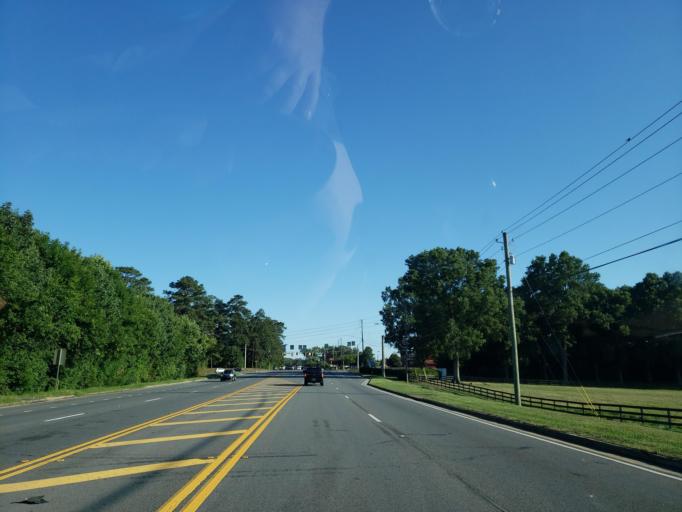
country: US
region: Georgia
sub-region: Floyd County
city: Rome
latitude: 34.2818
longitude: -85.1821
